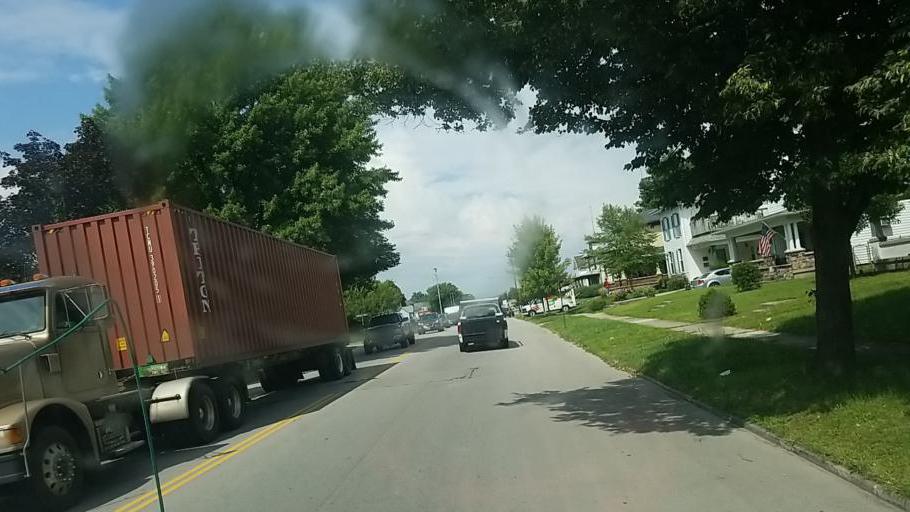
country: US
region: Ohio
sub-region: Champaign County
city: Urbana
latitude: 40.1177
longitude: -83.7507
